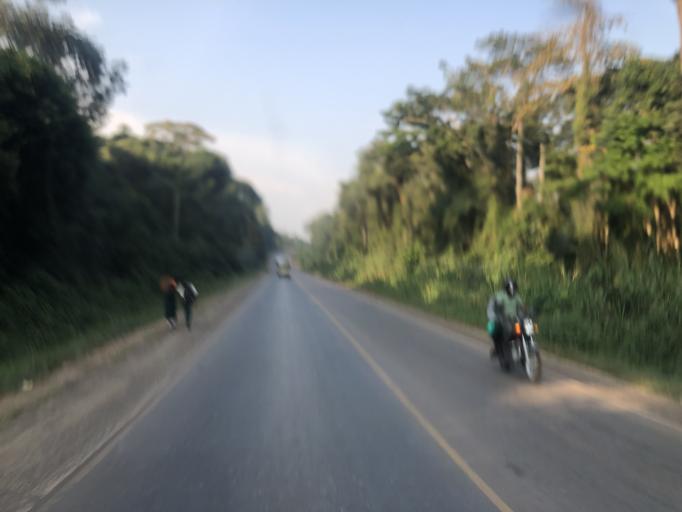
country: UG
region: Central Region
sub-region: Butambala District
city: Gombe
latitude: 0.1268
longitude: 32.2009
